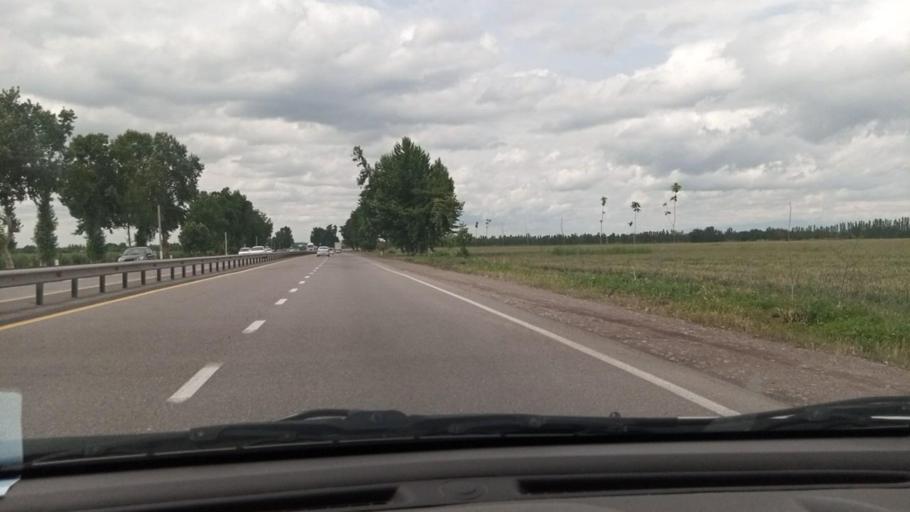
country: UZ
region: Toshkent Shahri
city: Bektemir
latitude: 41.1399
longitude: 69.4335
